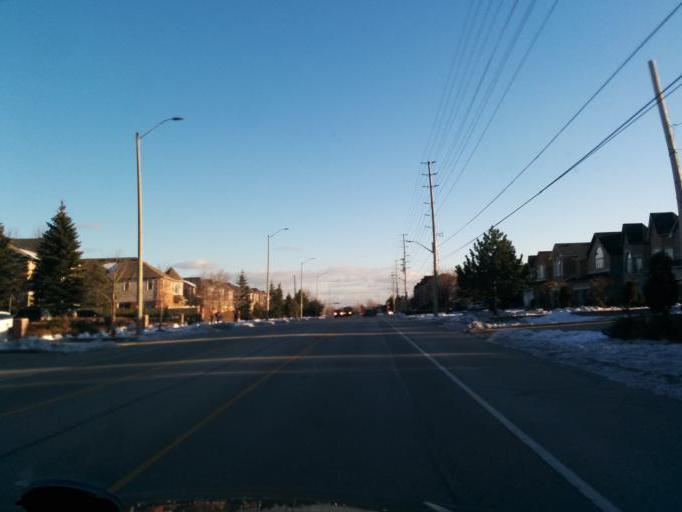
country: CA
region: Ontario
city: Mississauga
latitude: 43.5894
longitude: -79.6769
